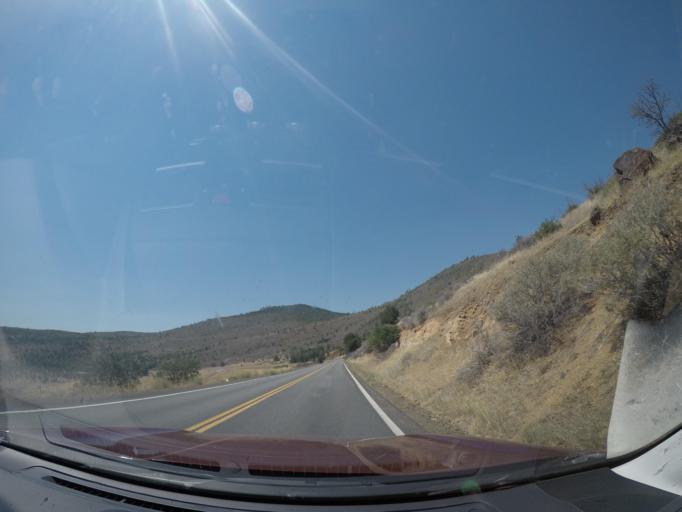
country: US
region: California
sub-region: Shasta County
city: Burney
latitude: 40.9991
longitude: -121.4999
